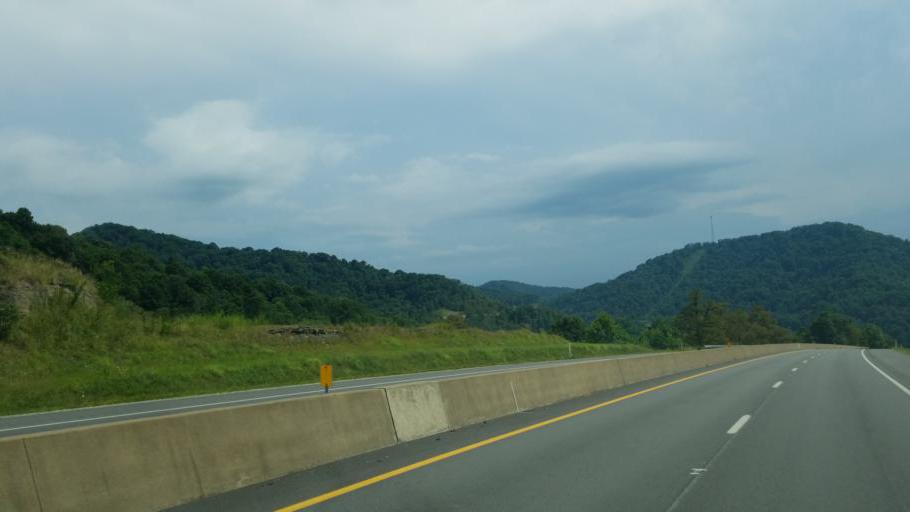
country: US
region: West Virginia
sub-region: Logan County
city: Chapmanville
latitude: 37.9081
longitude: -82.0385
